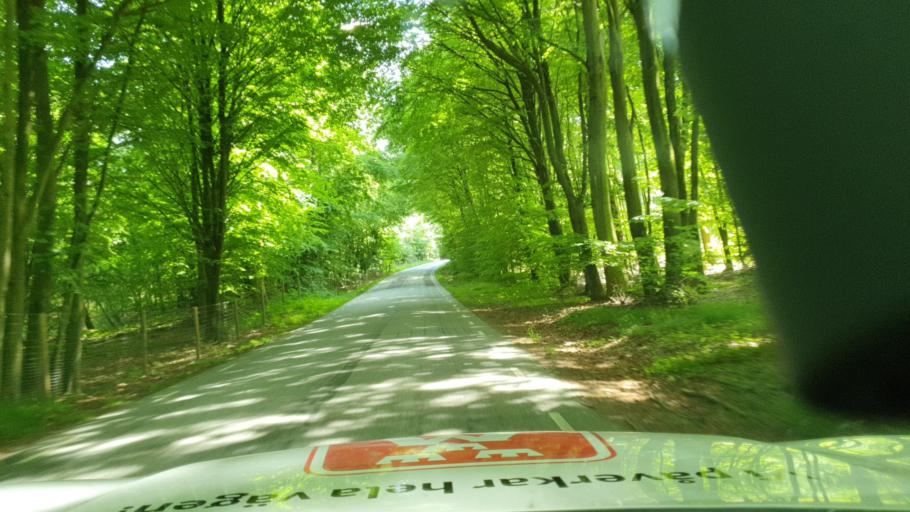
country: SE
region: Skane
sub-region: Svedala Kommun
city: Svedala
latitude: 55.5316
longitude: 13.2839
